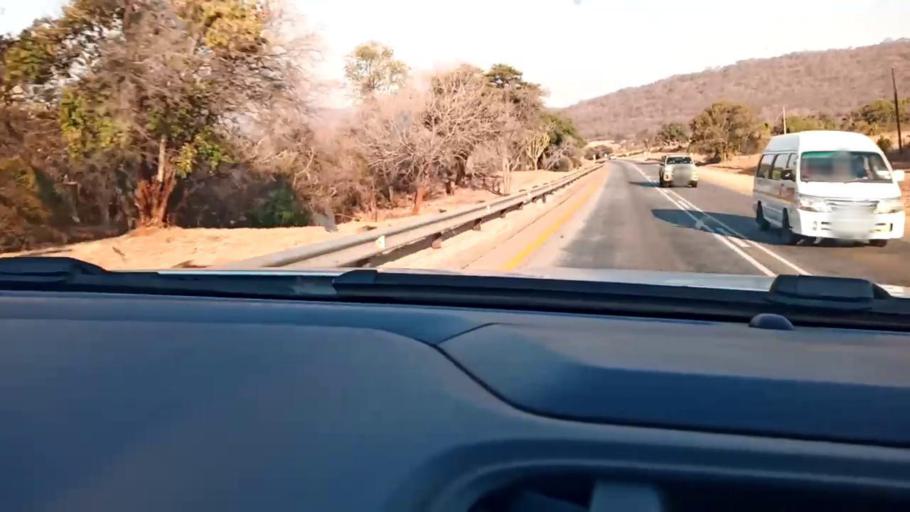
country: ZA
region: Limpopo
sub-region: Mopani District Municipality
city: Duiwelskloof
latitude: -23.6419
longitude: 30.1596
